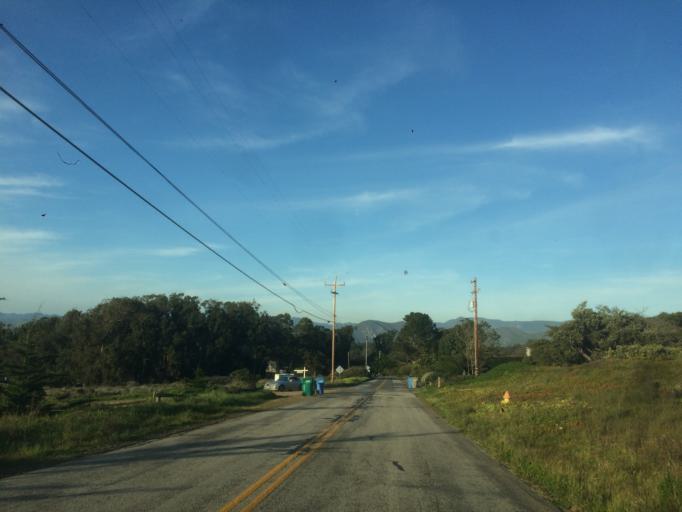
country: US
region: California
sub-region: San Luis Obispo County
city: Los Osos
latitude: 35.3062
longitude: -120.8582
